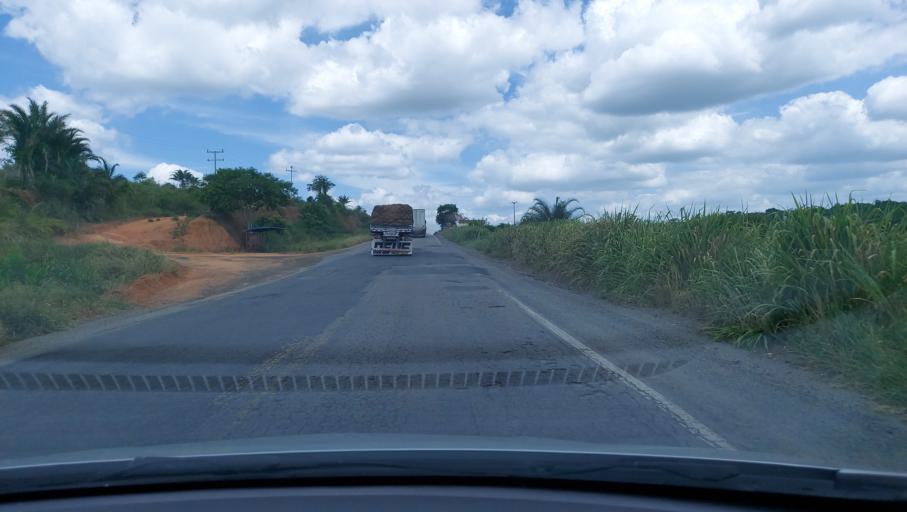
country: BR
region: Bahia
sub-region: Ruy Barbosa
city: Terra Nova
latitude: -12.4412
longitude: -40.7770
